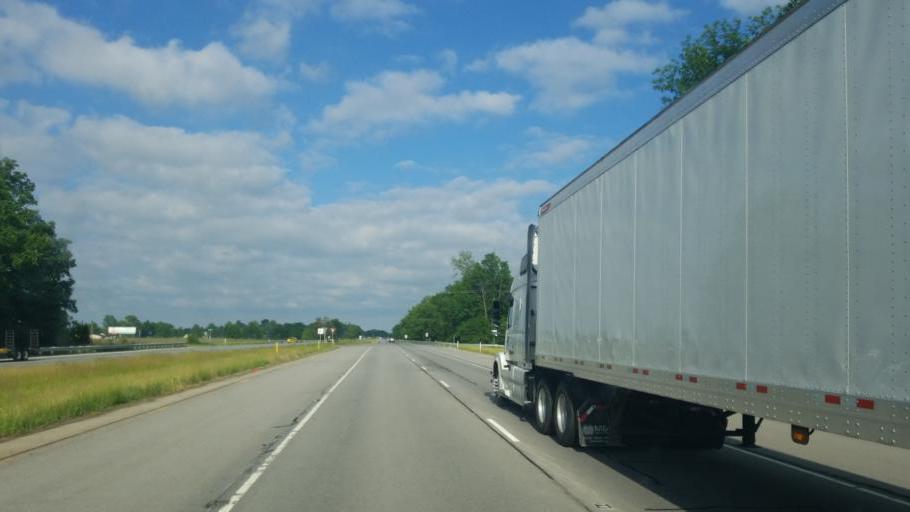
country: US
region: Indiana
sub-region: Whitley County
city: Churubusco
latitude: 41.1258
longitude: -85.3007
